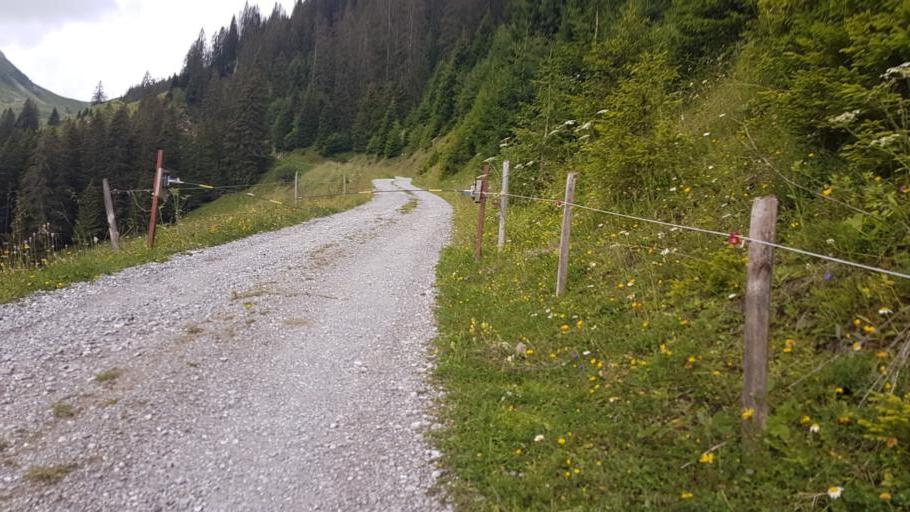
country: CH
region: Bern
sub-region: Obersimmental-Saanen District
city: Boltigen
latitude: 46.6908
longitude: 7.4356
